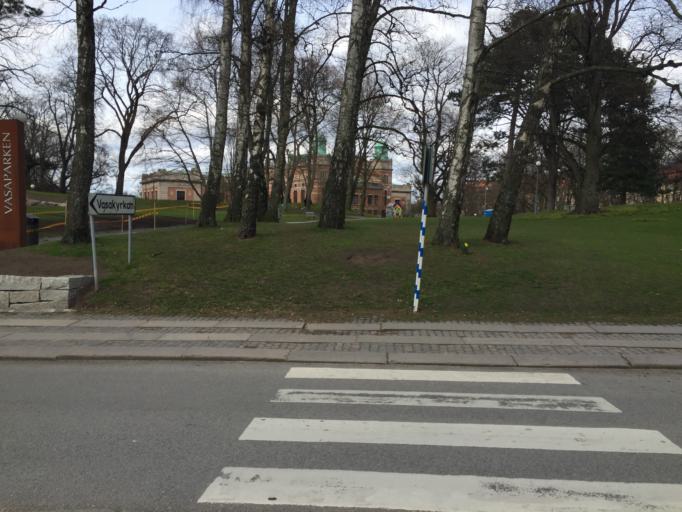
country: SE
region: Vaestra Goetaland
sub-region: Goteborg
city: Goeteborg
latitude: 57.6973
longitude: 11.9719
